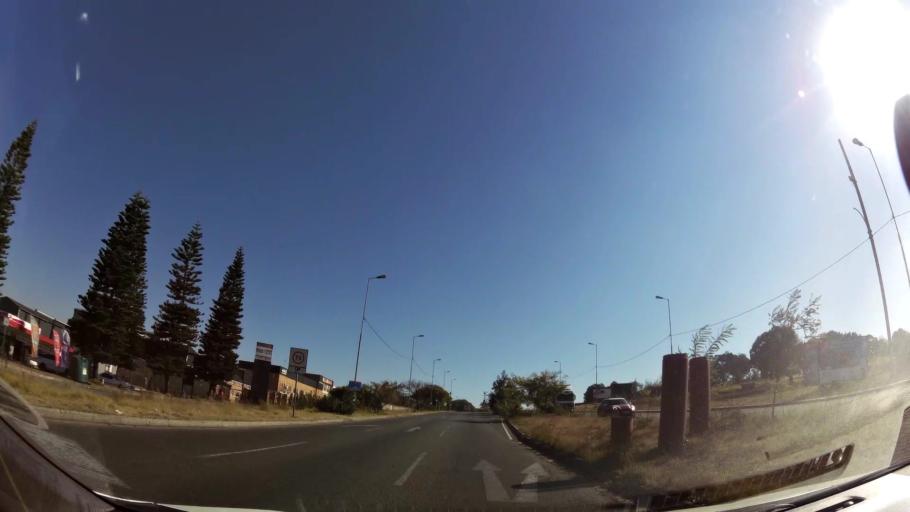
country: ZA
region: Gauteng
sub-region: Ekurhuleni Metropolitan Municipality
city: Germiston
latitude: -26.2509
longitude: 28.1091
